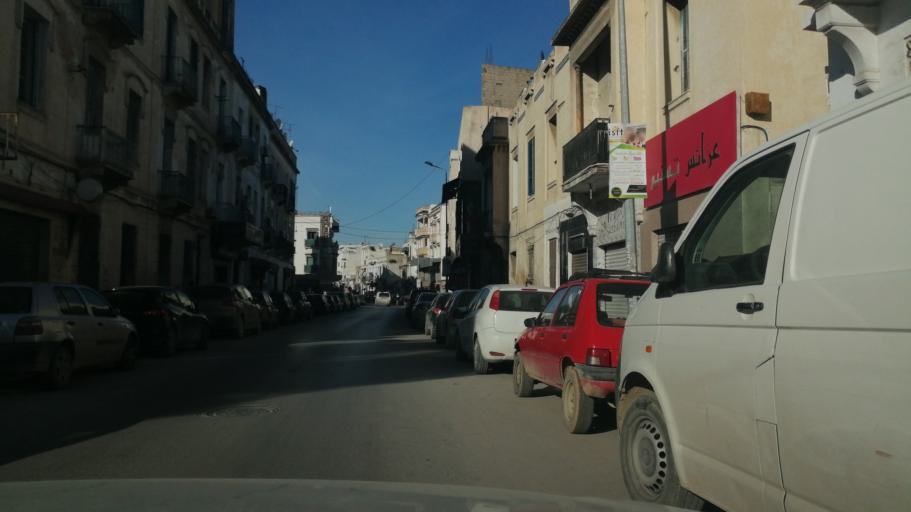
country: TN
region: Tunis
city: Tunis
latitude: 36.8057
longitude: 10.1733
